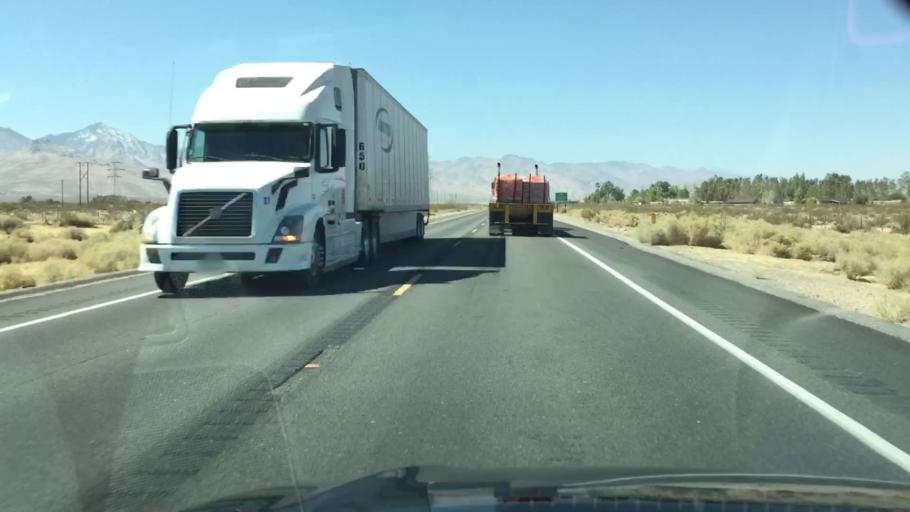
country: US
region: California
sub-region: Kern County
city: China Lake Acres
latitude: 35.6347
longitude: -117.7862
